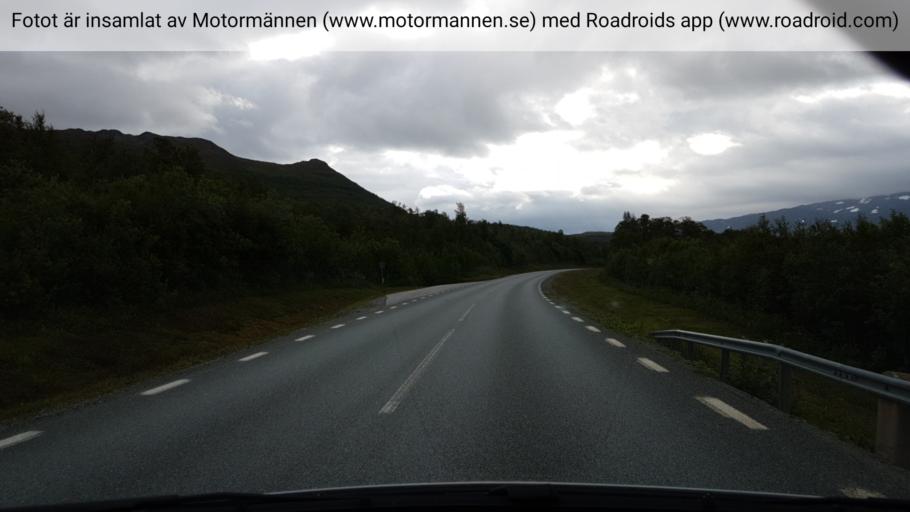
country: NO
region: Nordland
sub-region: Rana
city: Mo i Rana
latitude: 66.0837
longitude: 14.8634
